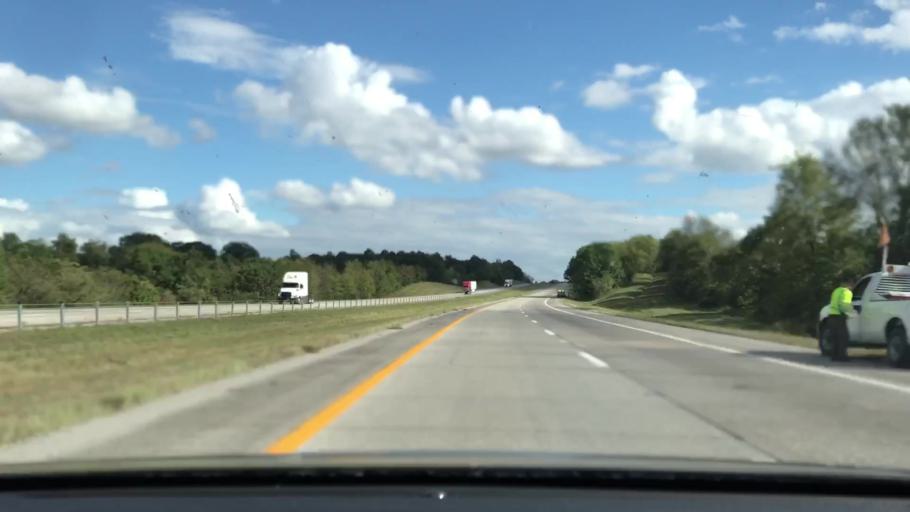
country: US
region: Kentucky
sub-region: Trigg County
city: Cadiz
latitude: 36.9072
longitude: -87.7751
